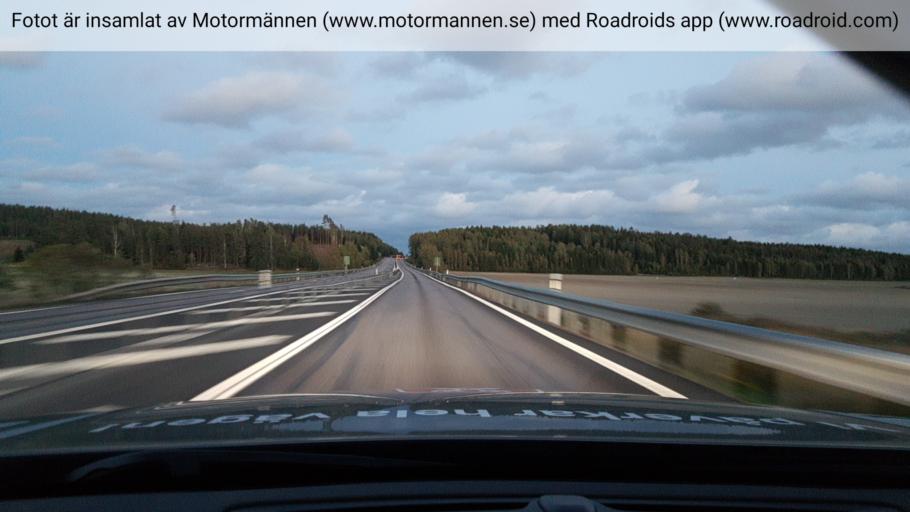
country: SE
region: Vaermland
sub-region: Karlstads Kommun
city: Skattkarr
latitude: 59.4022
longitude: 13.7841
